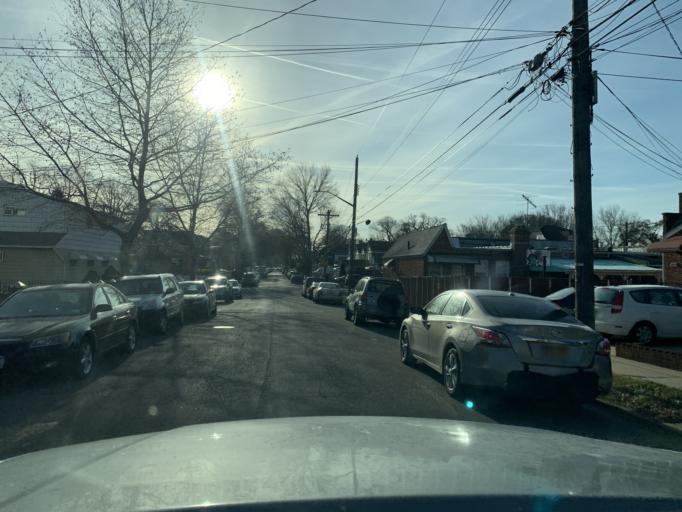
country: US
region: New York
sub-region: Queens County
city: Jamaica
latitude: 40.6996
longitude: -73.7806
